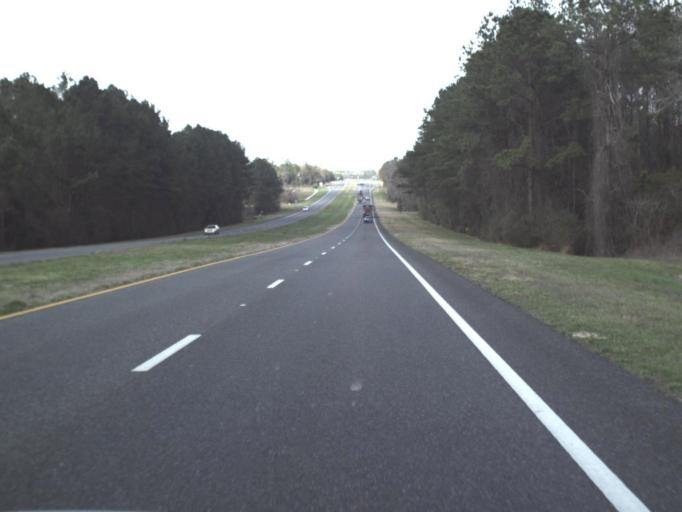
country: US
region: Florida
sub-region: Bay County
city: Youngstown
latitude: 30.5602
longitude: -85.3890
